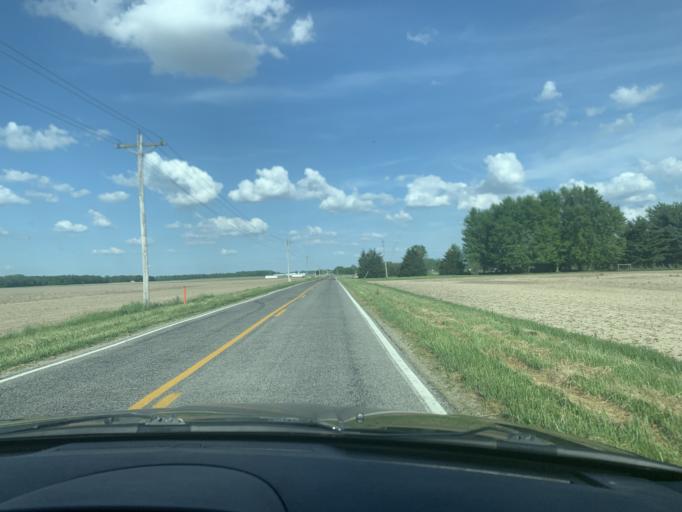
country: US
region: Ohio
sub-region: Logan County
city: De Graff
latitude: 40.2439
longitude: -84.0147
